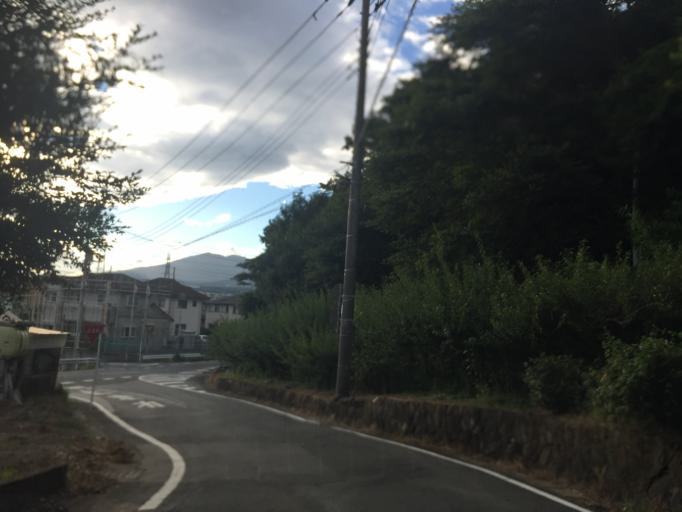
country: JP
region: Shizuoka
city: Mishima
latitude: 35.1541
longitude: 138.9102
